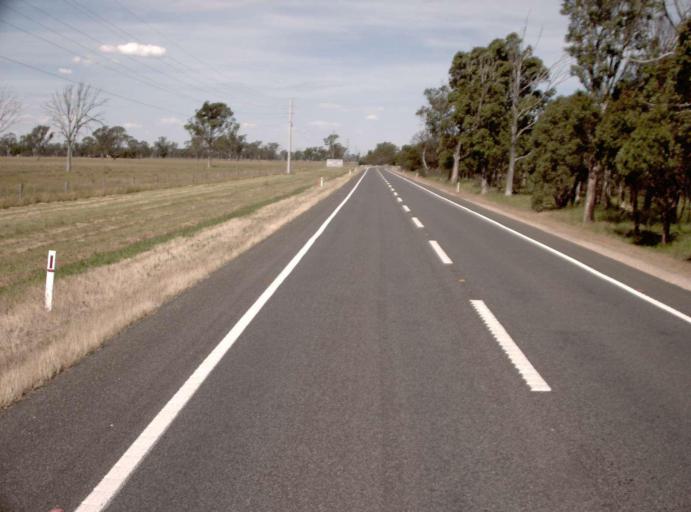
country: AU
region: Victoria
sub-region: East Gippsland
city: Bairnsdale
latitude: -37.8630
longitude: 147.5041
